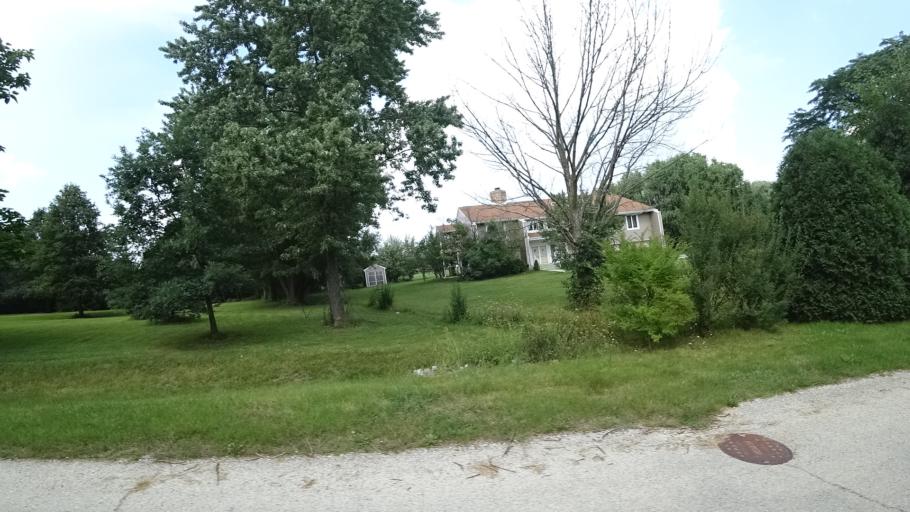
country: US
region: Illinois
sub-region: Will County
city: Goodings Grove
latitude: 41.6565
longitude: -87.8994
